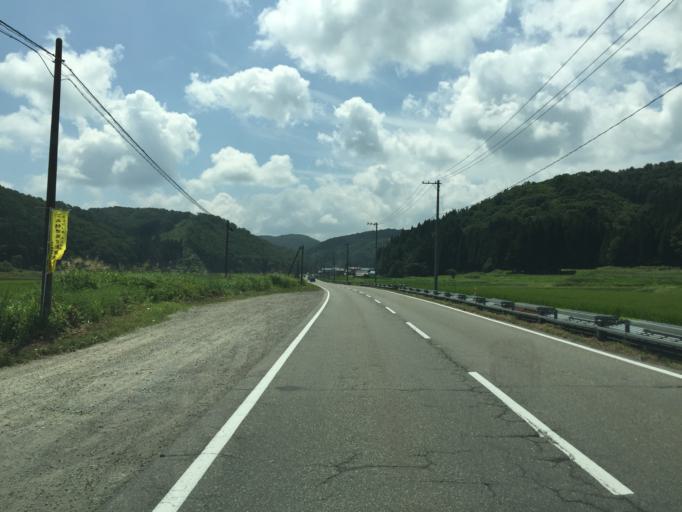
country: JP
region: Fukushima
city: Inawashiro
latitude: 37.4419
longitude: 140.0198
